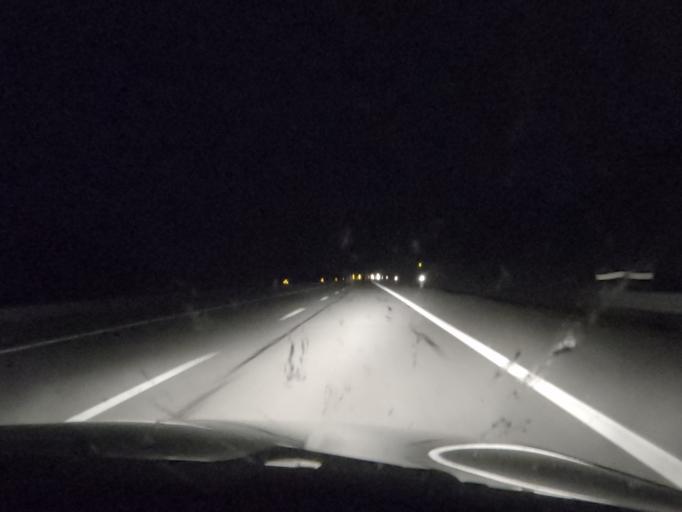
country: PT
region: Evora
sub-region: Estremoz
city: Estremoz
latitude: 38.8321
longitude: -7.6118
